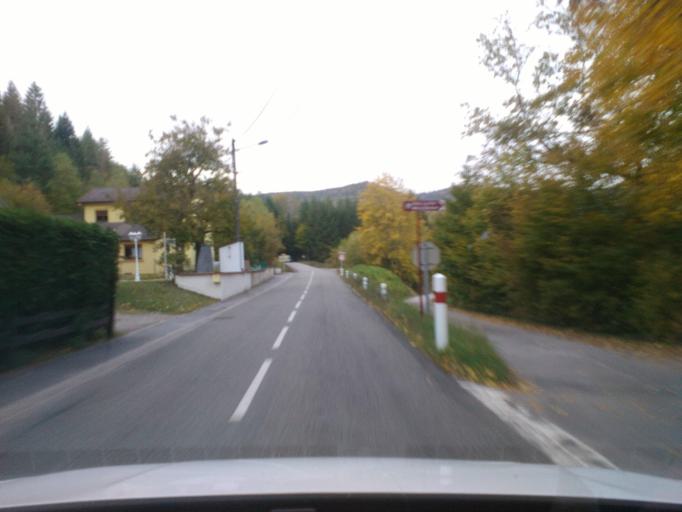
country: FR
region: Lorraine
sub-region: Departement des Vosges
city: Saint-Ame
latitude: 48.0325
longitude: 6.6735
